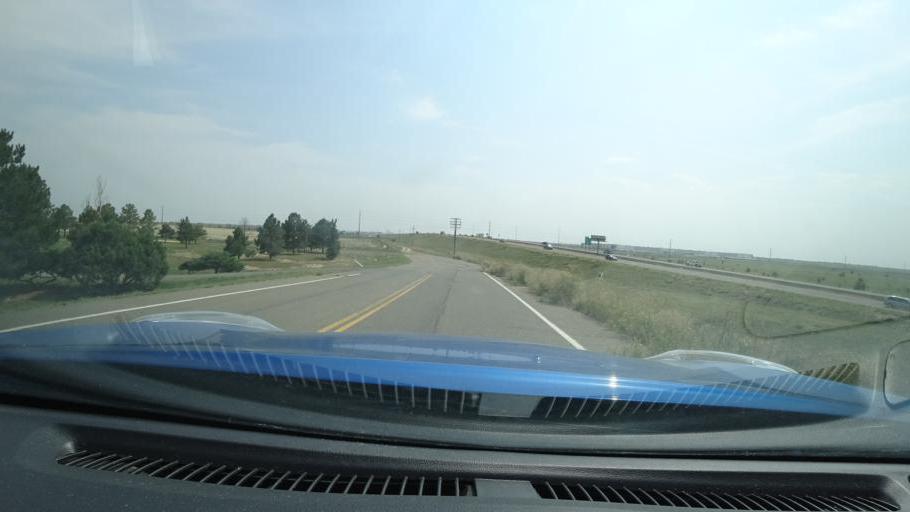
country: US
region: Colorado
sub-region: Adams County
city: Aurora
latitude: 39.7540
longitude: -104.7156
